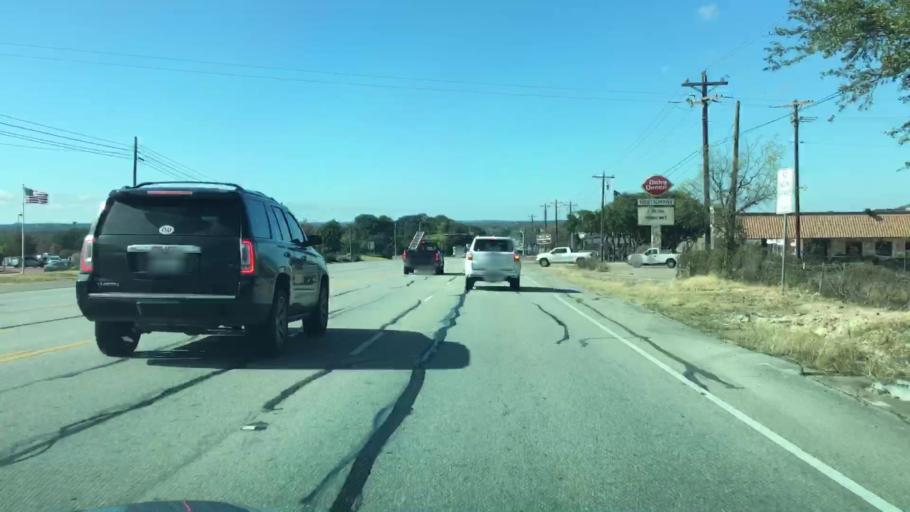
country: US
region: Texas
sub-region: Hays County
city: Dripping Springs
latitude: 30.1924
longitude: -98.0820
